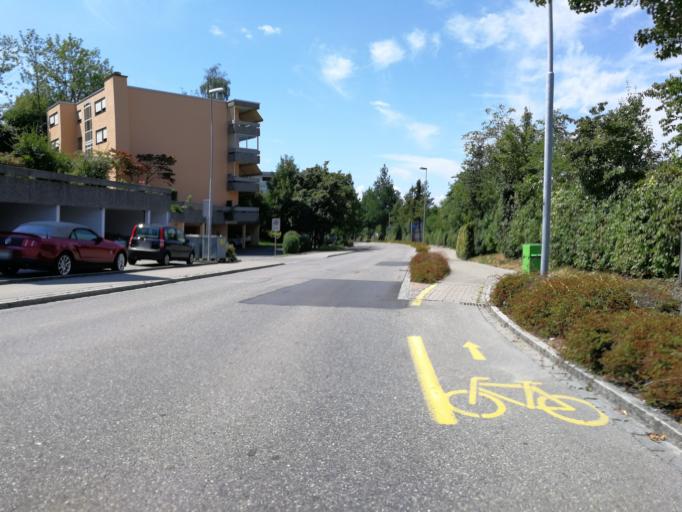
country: CH
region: Zurich
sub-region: Bezirk Hinwil
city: Wetzikon / Kempten
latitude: 47.3318
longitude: 8.8167
